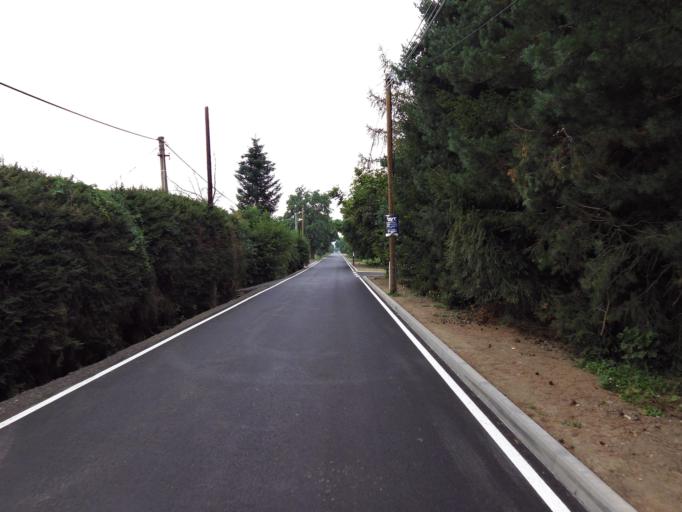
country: CZ
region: Central Bohemia
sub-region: Okres Benesov
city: Pysely
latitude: 49.8727
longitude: 14.6940
